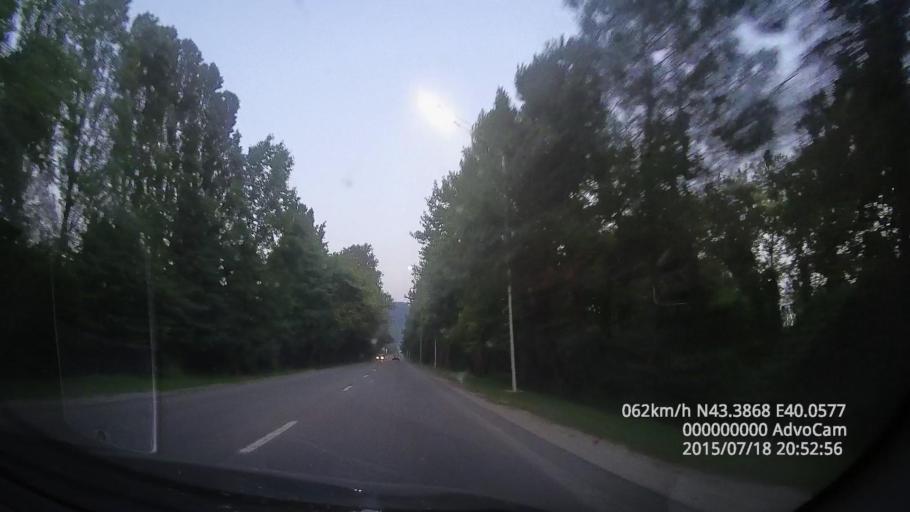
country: GE
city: Gantiadi
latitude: 43.3866
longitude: 40.0591
